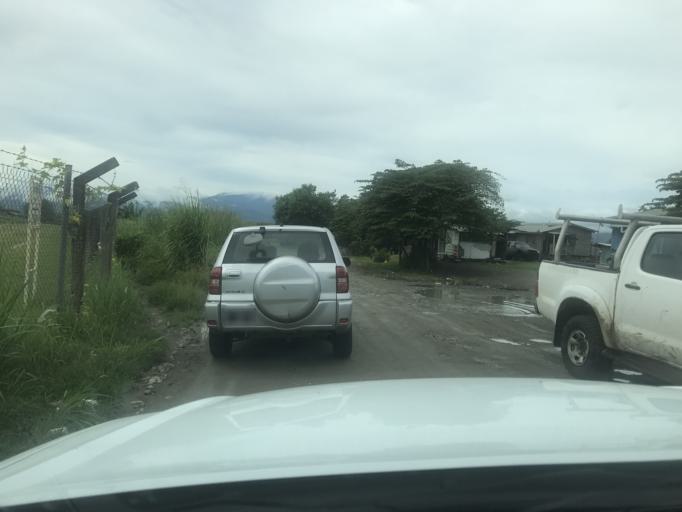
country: SB
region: Guadalcanal
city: Honiara
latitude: -9.4340
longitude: 160.0362
